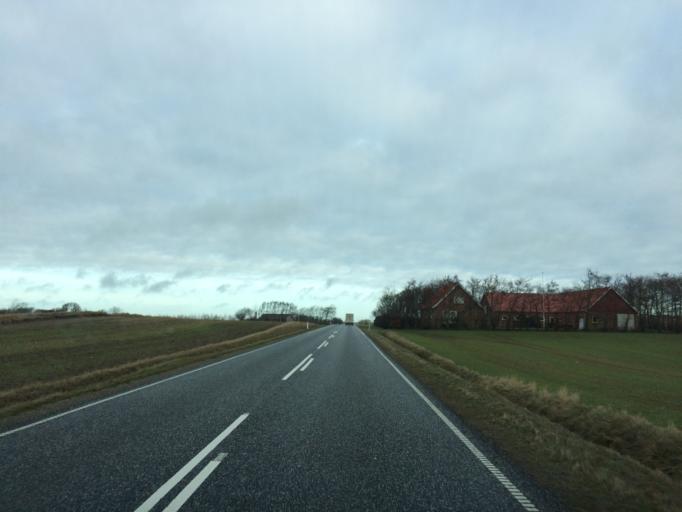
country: DK
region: Central Jutland
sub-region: Struer Kommune
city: Struer
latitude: 56.4443
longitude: 8.5332
